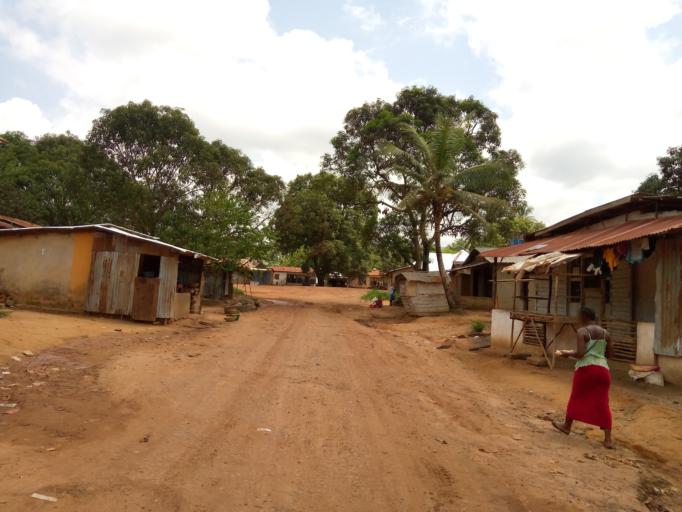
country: SL
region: Western Area
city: Waterloo
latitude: 8.3892
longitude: -12.9483
